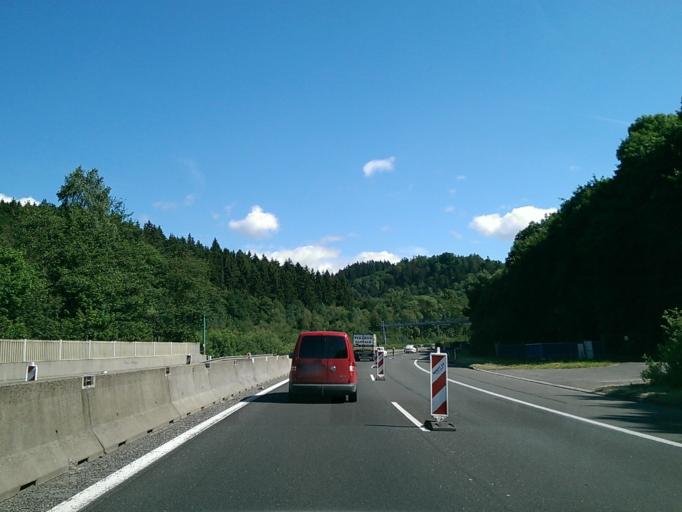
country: CZ
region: Liberecky
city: Hodkovice nad Mohelkou
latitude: 50.6721
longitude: 15.0954
